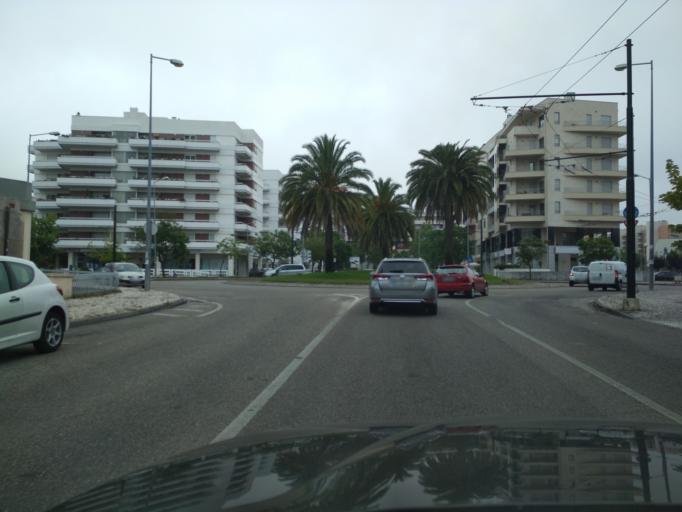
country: PT
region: Coimbra
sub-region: Coimbra
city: Coimbra
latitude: 40.2027
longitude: -8.4048
